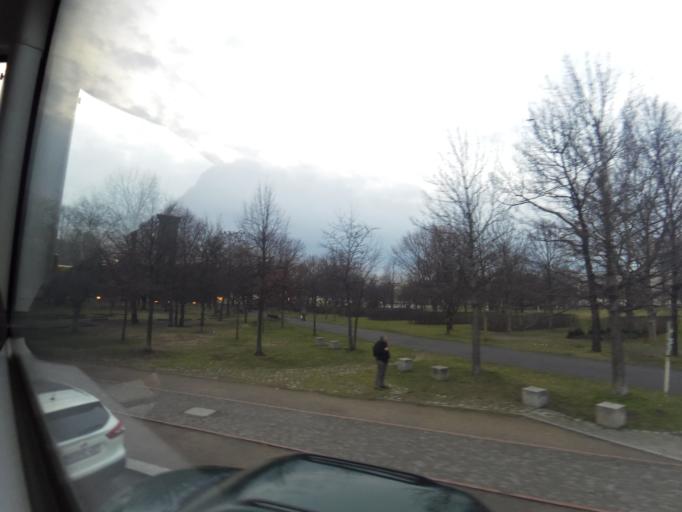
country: DE
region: Berlin
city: Friedrichshagen
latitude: 52.4566
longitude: 13.6142
